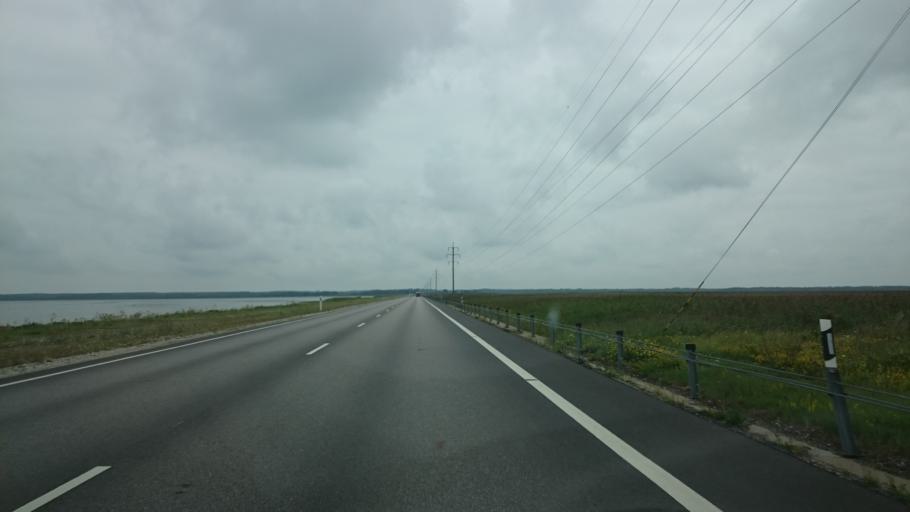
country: EE
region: Saare
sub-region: Orissaare vald
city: Orissaare
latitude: 58.5549
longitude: 23.1454
